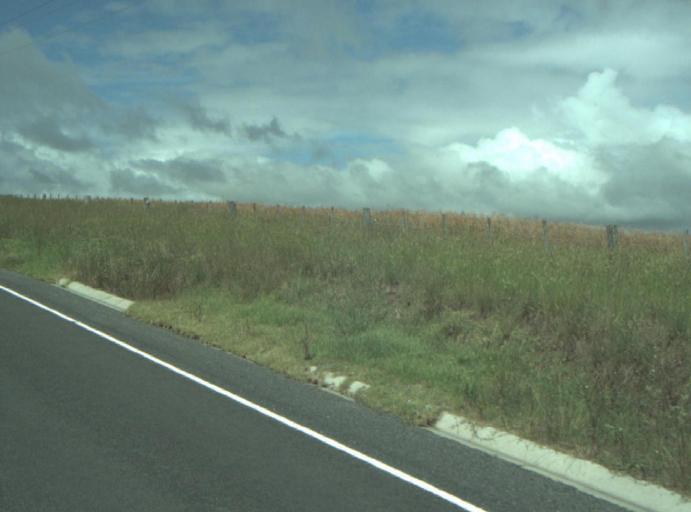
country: AU
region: Victoria
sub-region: Greater Geelong
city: Wandana Heights
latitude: -38.1819
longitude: 144.2700
